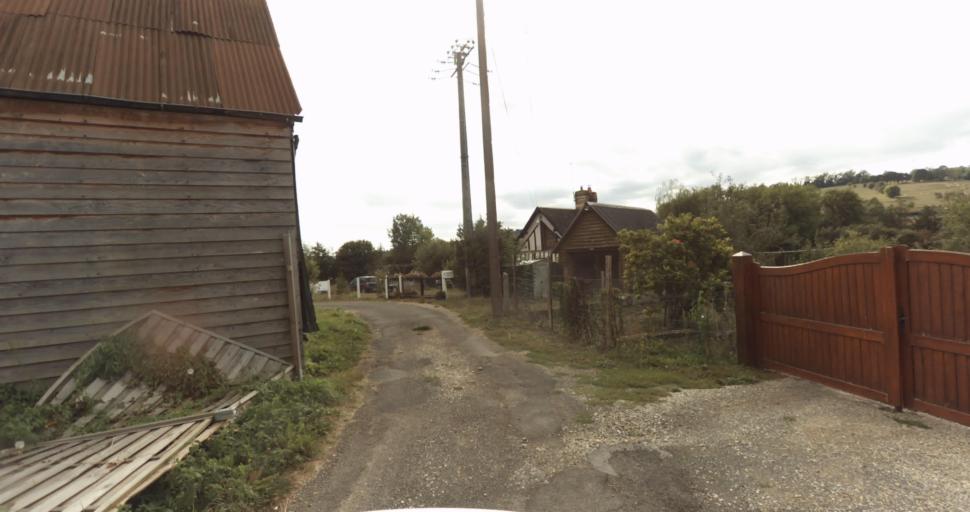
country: FR
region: Lower Normandy
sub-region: Departement de l'Orne
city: Vimoutiers
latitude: 48.9192
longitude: 0.2065
